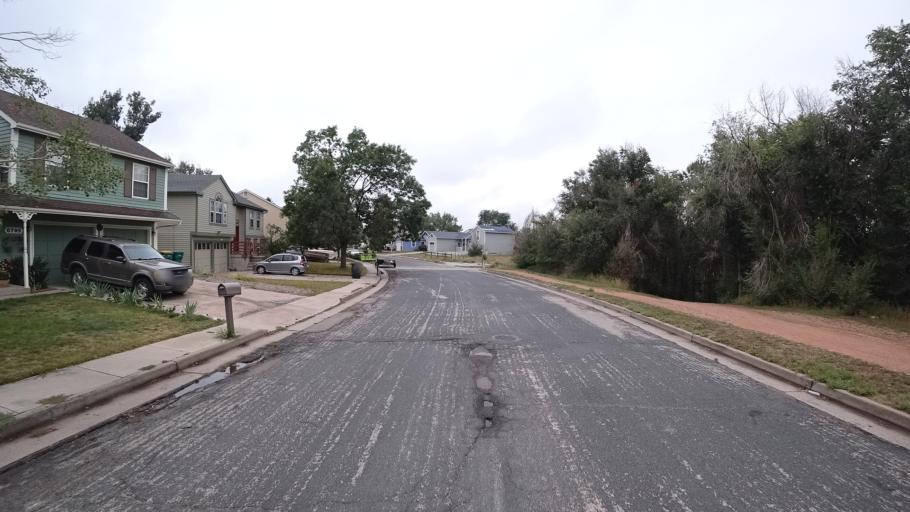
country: US
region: Colorado
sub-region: El Paso County
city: Cimarron Hills
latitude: 38.9294
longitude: -104.7645
